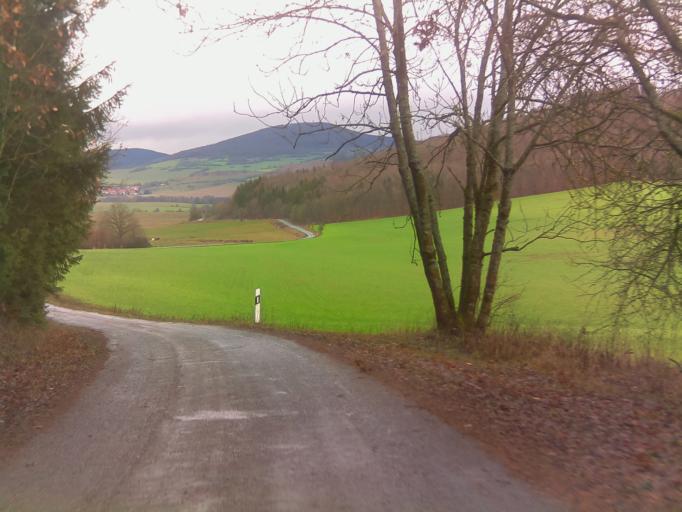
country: DE
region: Bavaria
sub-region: Regierungsbezirk Unterfranken
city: Willmars
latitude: 50.5393
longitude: 10.2388
